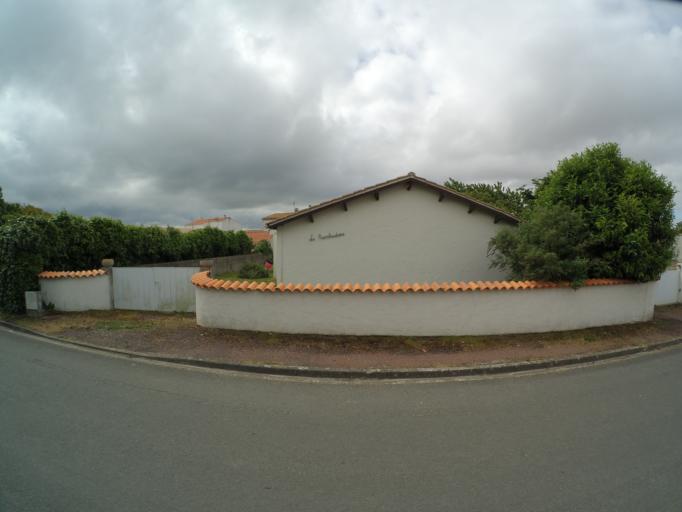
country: FR
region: Poitou-Charentes
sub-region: Departement de la Charente-Maritime
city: Yves
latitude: 46.0203
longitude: -1.0468
